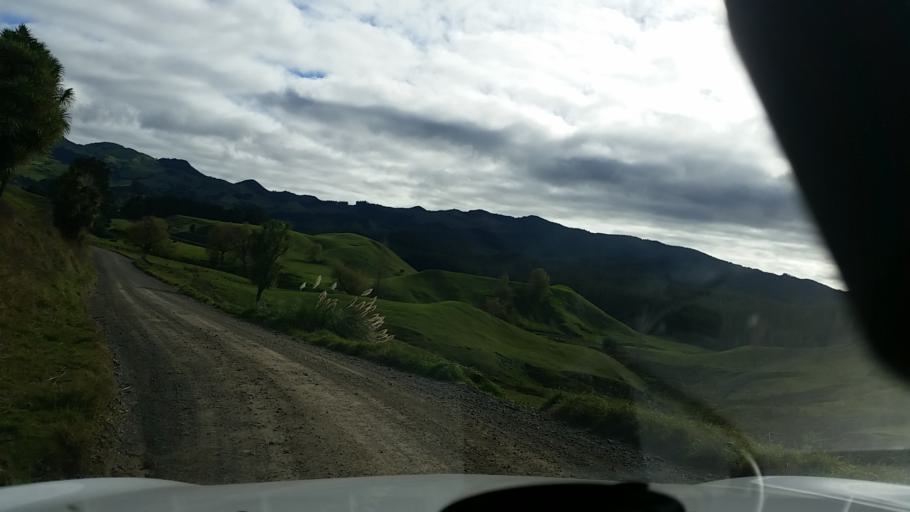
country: NZ
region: Hawke's Bay
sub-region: Napier City
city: Napier
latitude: -39.1097
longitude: 176.8937
